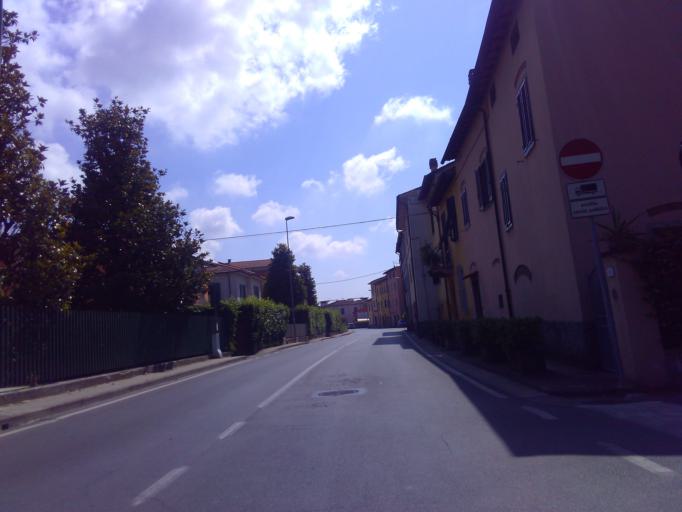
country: IT
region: Tuscany
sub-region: Provincia di Lucca
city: Lucca
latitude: 43.8415
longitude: 10.4838
